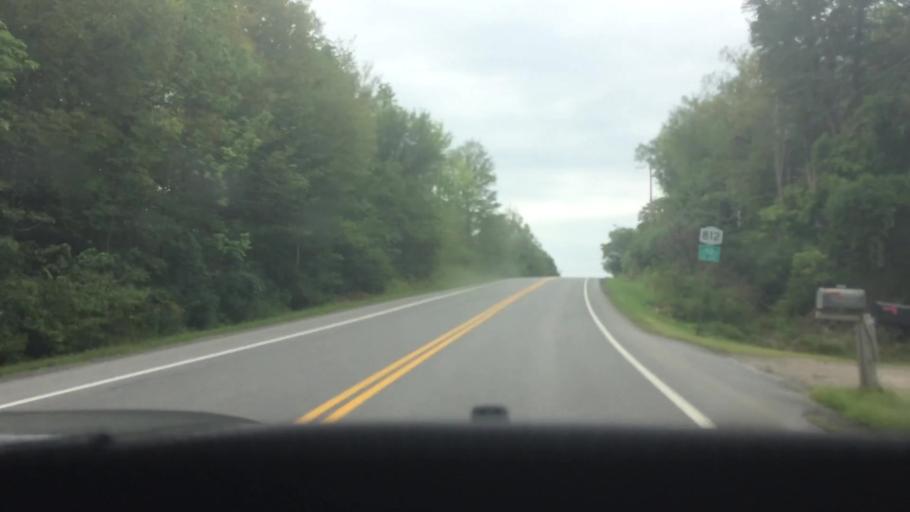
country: US
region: New York
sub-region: St. Lawrence County
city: Canton
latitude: 44.5177
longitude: -75.3383
